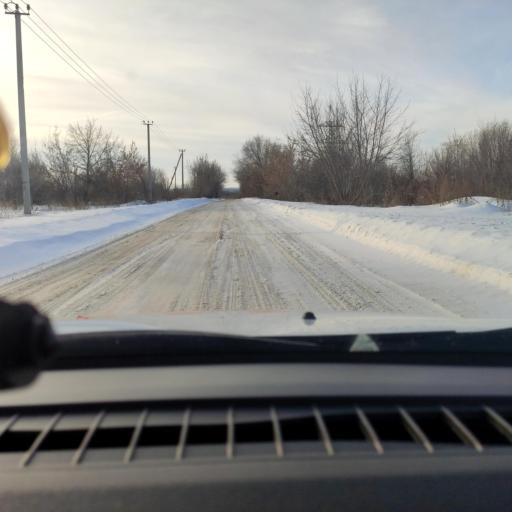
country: RU
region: Samara
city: Chapayevsk
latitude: 52.9927
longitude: 49.7357
